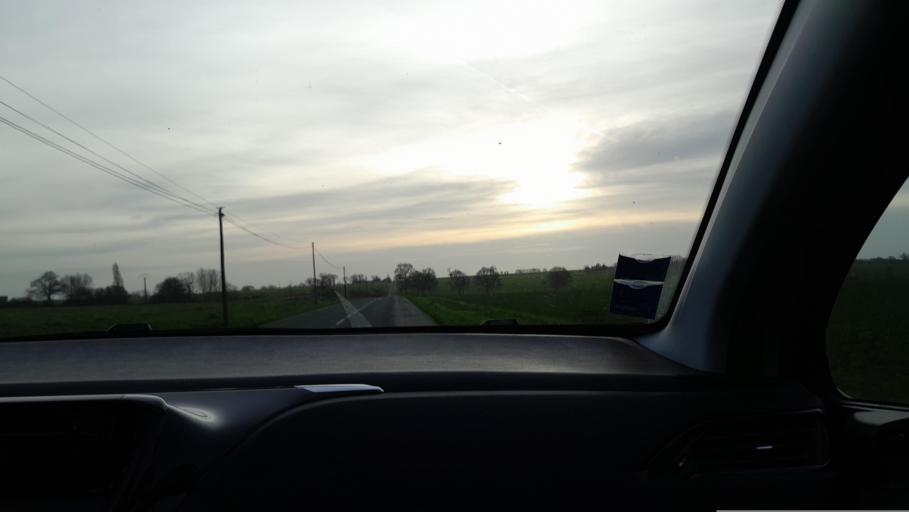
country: FR
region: Pays de la Loire
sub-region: Departement de la Mayenne
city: Ballots
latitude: 47.8773
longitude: -1.0130
